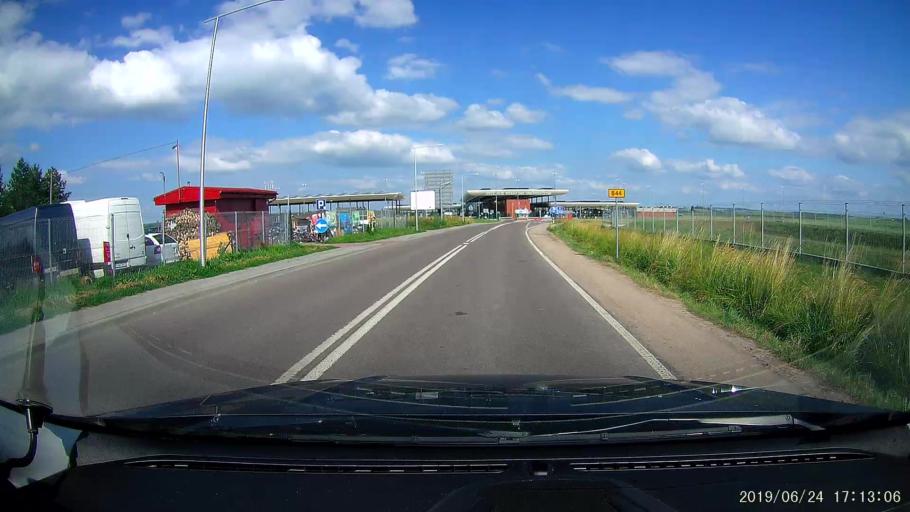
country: PL
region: Lublin Voivodeship
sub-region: Powiat hrubieszowski
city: Dolhobyczow
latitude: 50.5783
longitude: 24.0825
